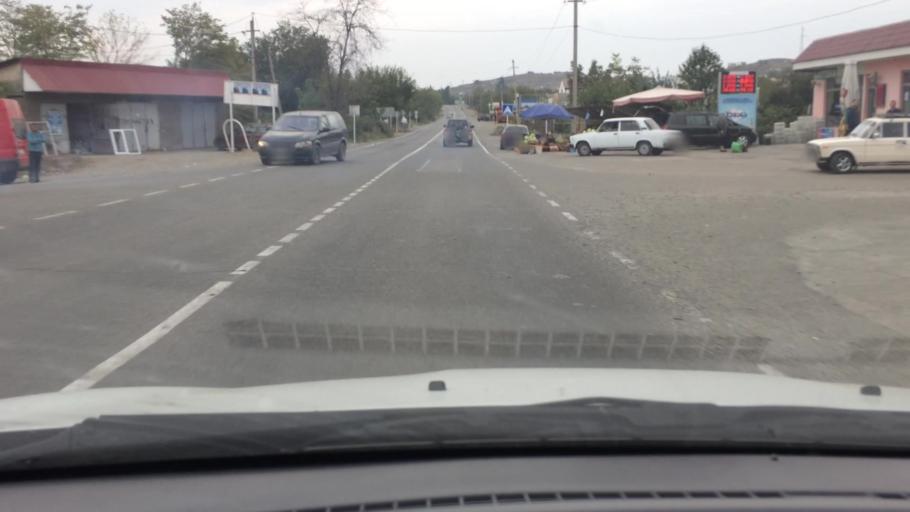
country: GE
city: Naghvarevi
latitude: 41.3765
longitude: 44.8339
